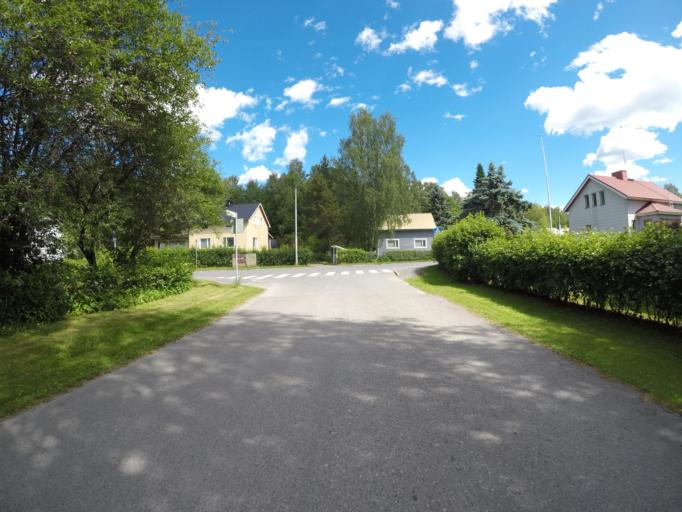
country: FI
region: Haeme
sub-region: Haemeenlinna
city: Haemeenlinna
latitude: 61.0118
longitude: 24.4315
